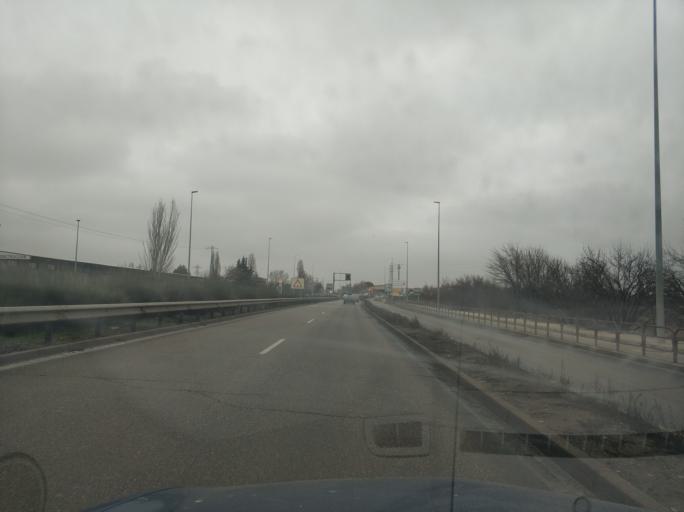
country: ES
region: Castille and Leon
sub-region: Provincia de Valladolid
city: Cisterniga
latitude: 41.6300
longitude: -4.7023
